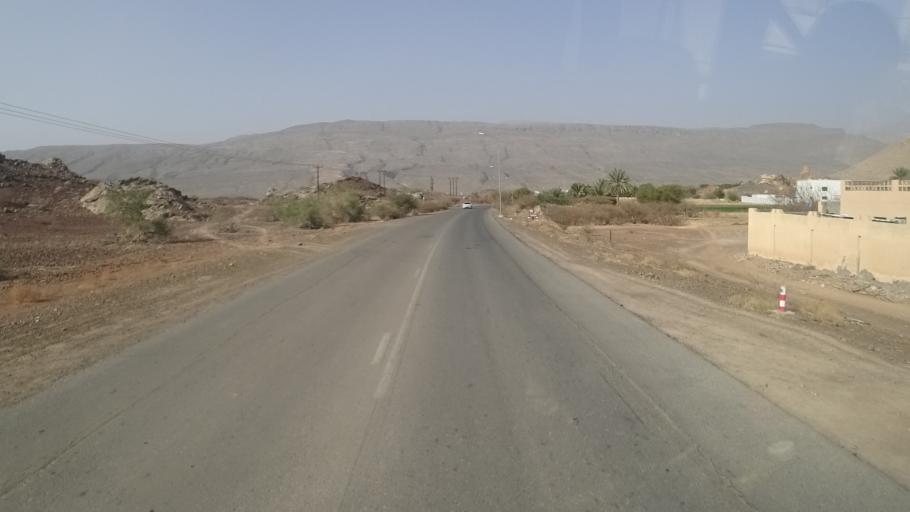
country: OM
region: Muhafazat ad Dakhiliyah
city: Bahla'
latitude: 23.0451
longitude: 57.4266
